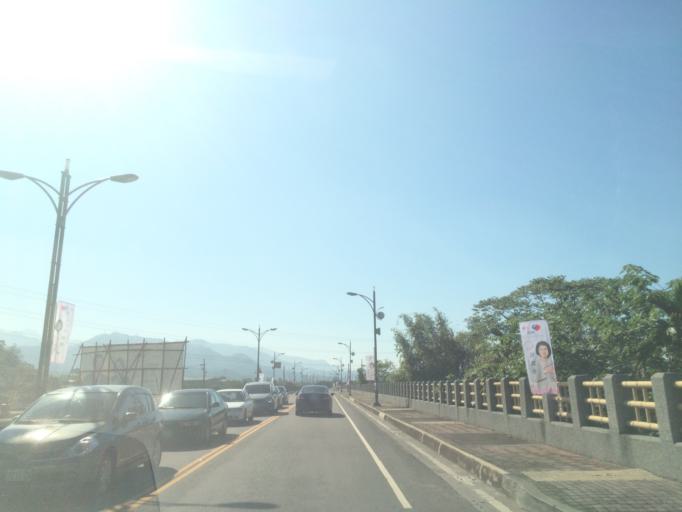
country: TW
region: Taiwan
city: Lugu
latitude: 23.7953
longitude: 120.7077
